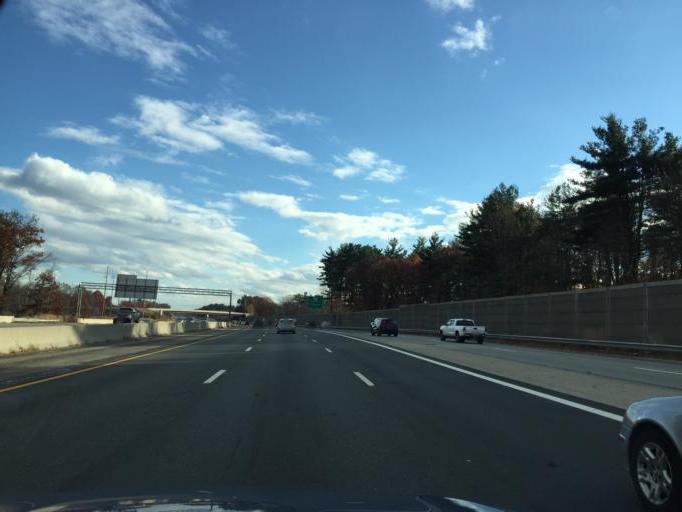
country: US
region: Massachusetts
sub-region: Middlesex County
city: Lowell
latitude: 42.6036
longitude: -71.3242
